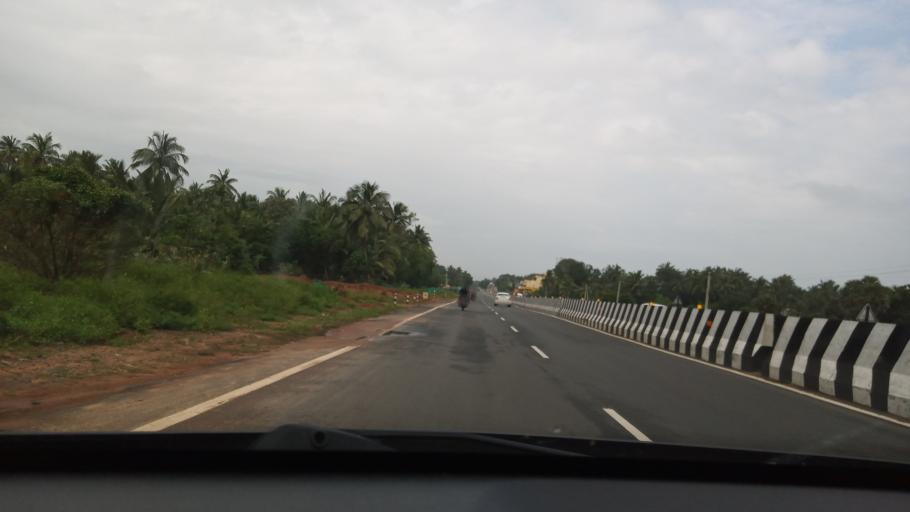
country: IN
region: Tamil Nadu
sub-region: Villupuram
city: Auroville
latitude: 12.0013
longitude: 79.8531
